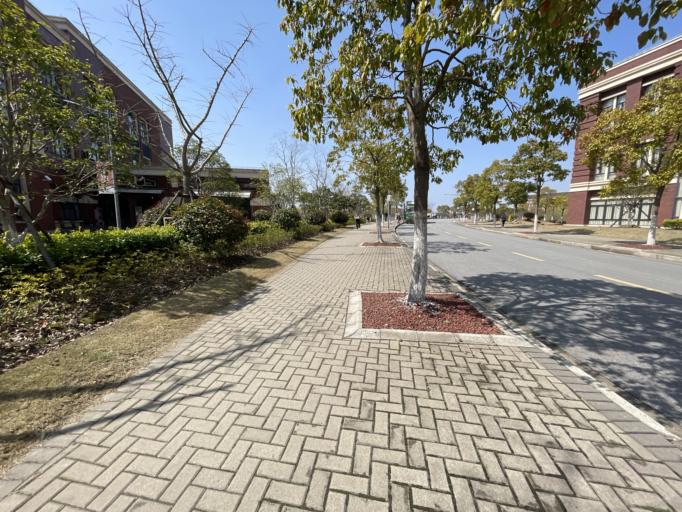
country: CN
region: Shanghai Shi
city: Shuyuan
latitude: 30.8923
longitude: 121.8864
